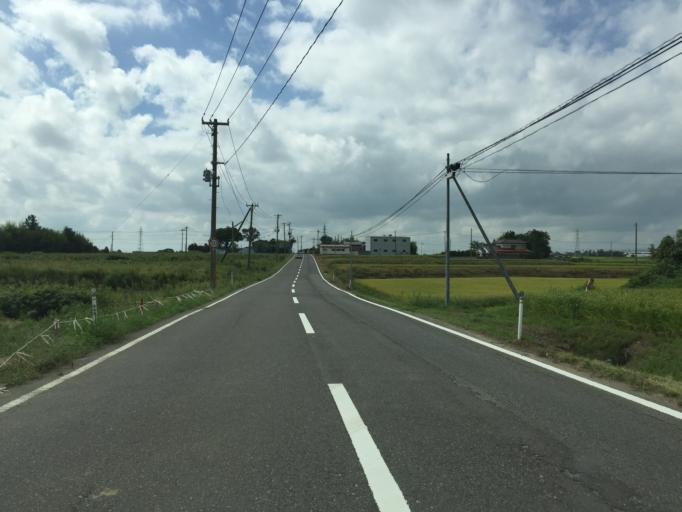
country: JP
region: Fukushima
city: Motomiya
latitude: 37.4651
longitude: 140.3403
